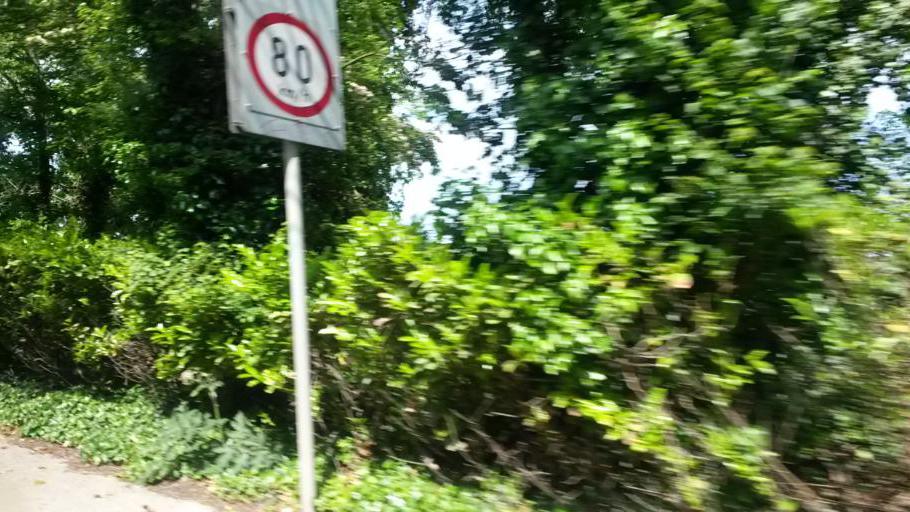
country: IE
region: Leinster
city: Donabate
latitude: 53.4892
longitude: -6.1657
